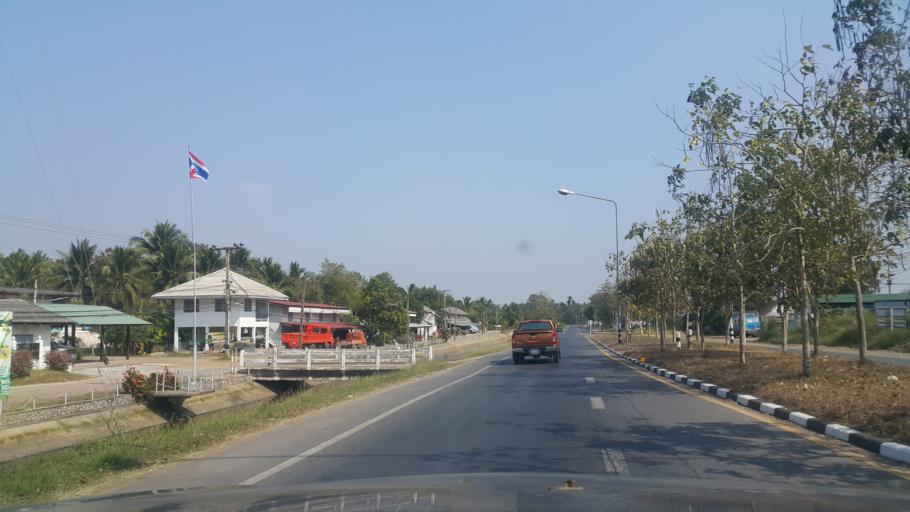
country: TH
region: Nakhon Ratchasima
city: Pak Thong Chai
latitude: 14.6933
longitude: 102.0197
